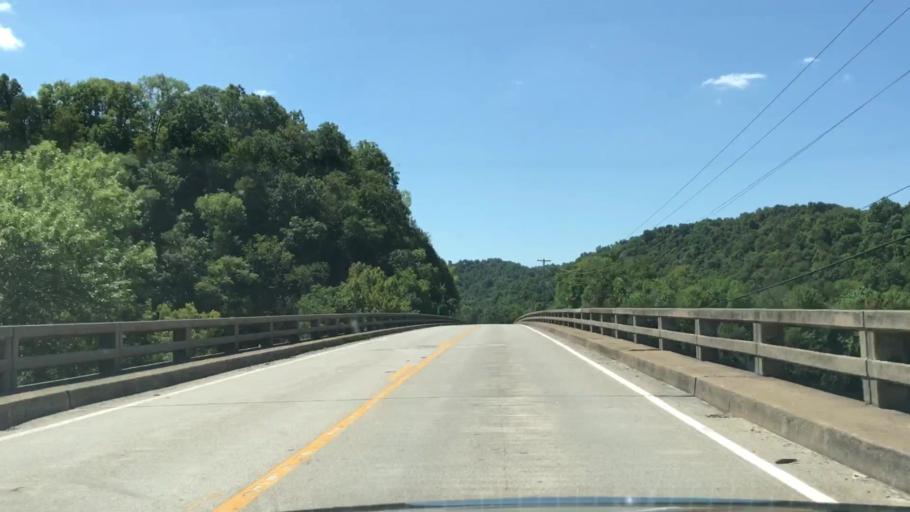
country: US
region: Kentucky
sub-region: Cumberland County
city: Burkesville
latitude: 36.7470
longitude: -85.3716
